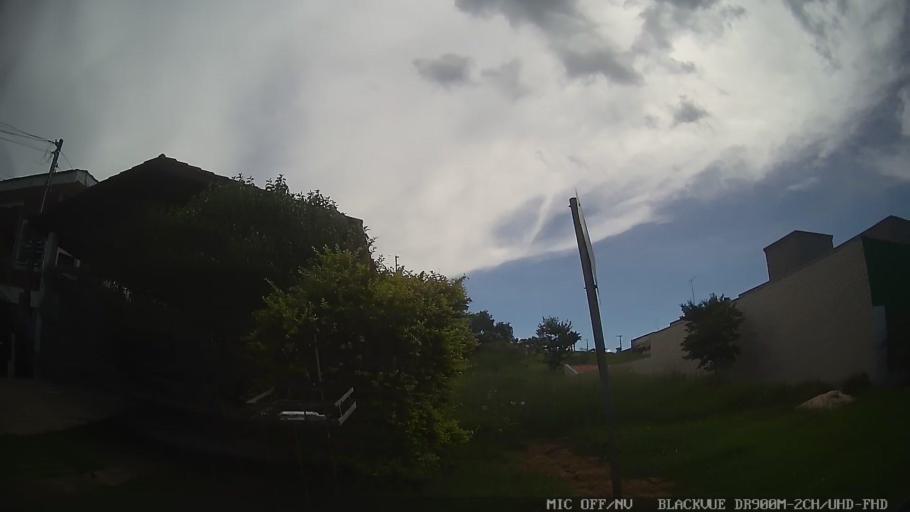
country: BR
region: Sao Paulo
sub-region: Conchas
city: Conchas
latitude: -23.0178
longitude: -48.0018
